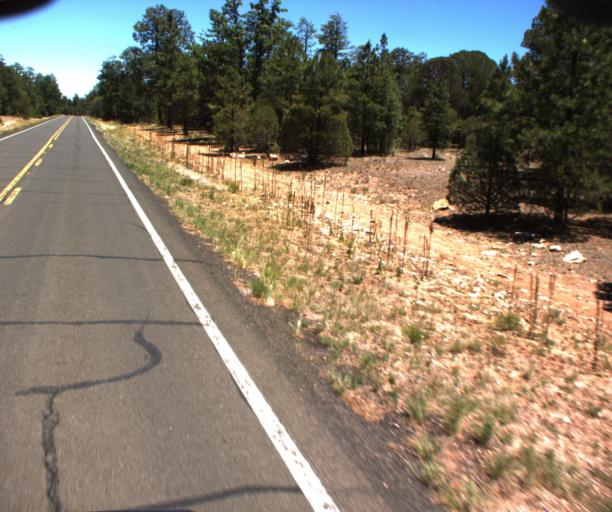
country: US
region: Arizona
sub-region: Gila County
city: Star Valley
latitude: 34.6284
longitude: -111.1210
